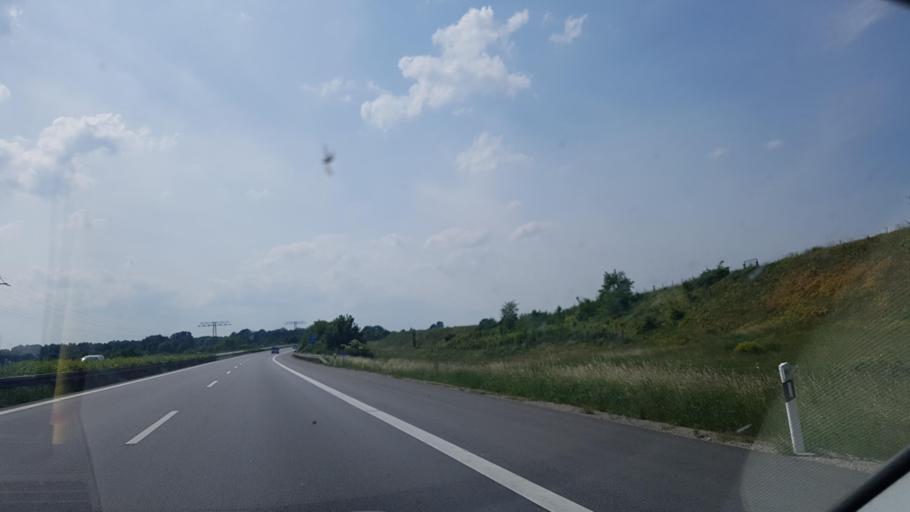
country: DE
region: Saxony
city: Bautzen
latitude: 51.1900
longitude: 14.3805
